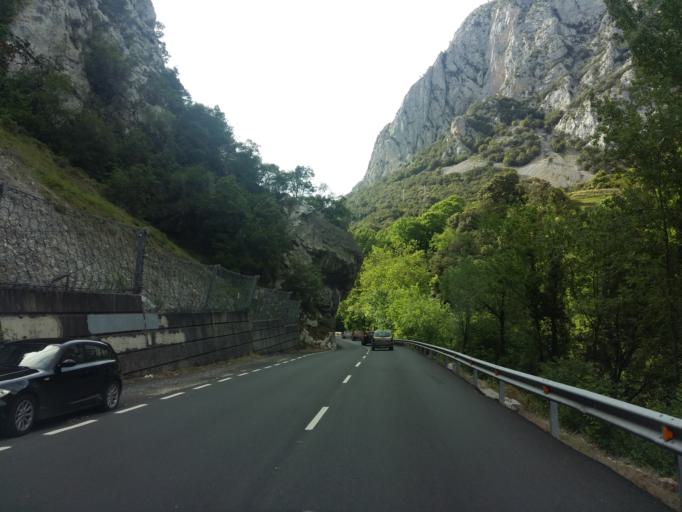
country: ES
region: Cantabria
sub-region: Provincia de Cantabria
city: Tresviso
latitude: 43.2503
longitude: -4.6021
